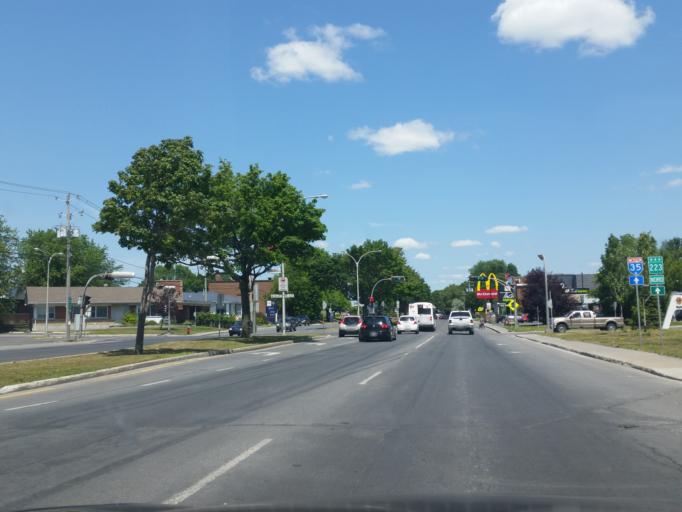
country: CA
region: Quebec
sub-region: Monteregie
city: Saint-Jean-sur-Richelieu
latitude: 45.3184
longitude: -73.2639
